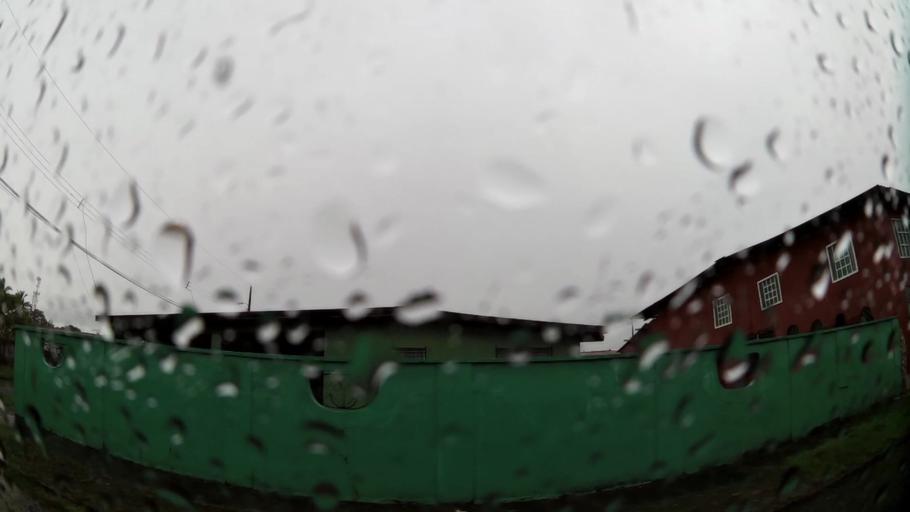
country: PA
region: Colon
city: Puerto Pilon
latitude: 9.3558
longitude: -79.7955
